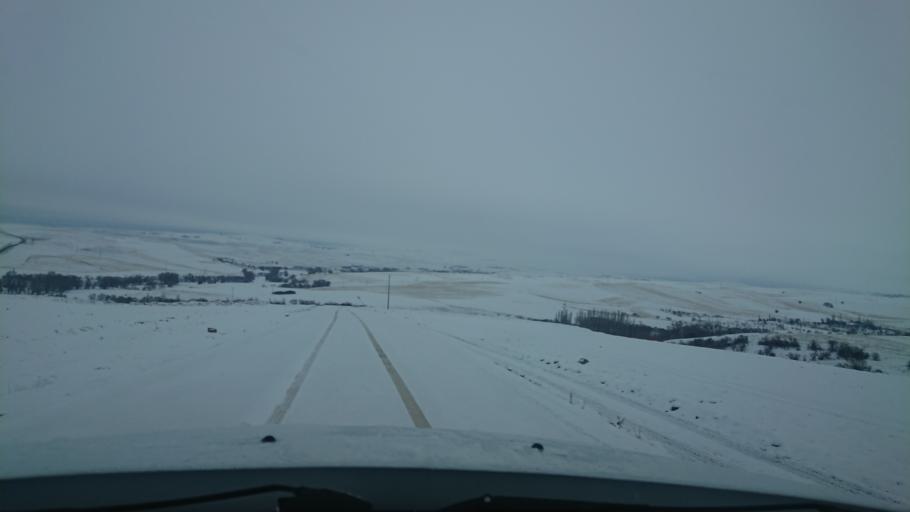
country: TR
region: Aksaray
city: Agacoren
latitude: 38.7529
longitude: 33.8757
